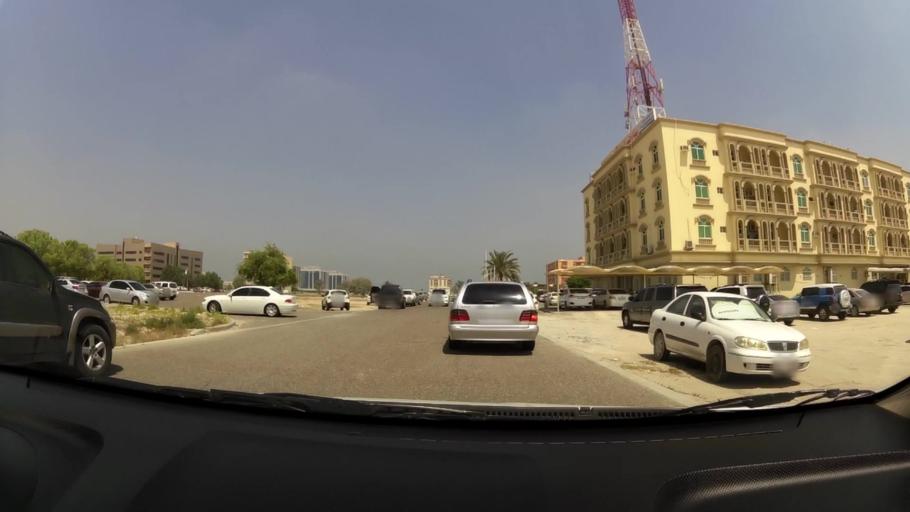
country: AE
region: Umm al Qaywayn
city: Umm al Qaywayn
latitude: 25.5764
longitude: 55.5625
